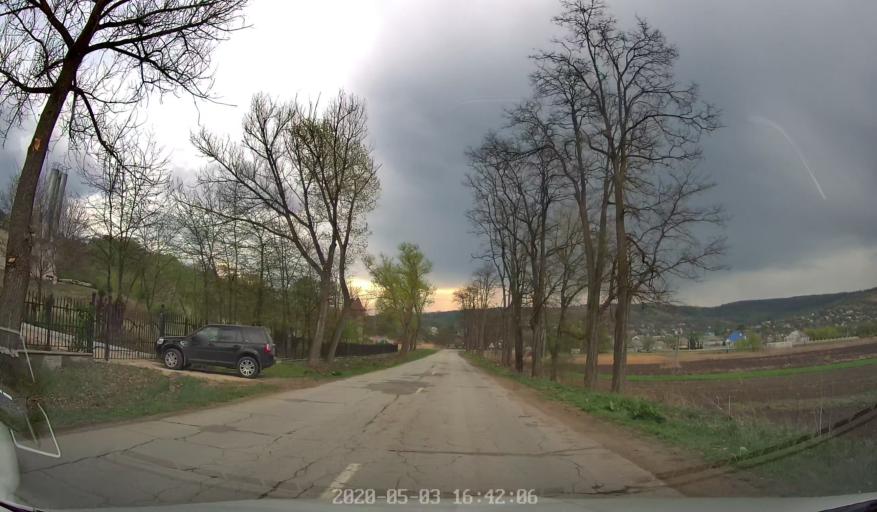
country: MD
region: Stinga Nistrului
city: Bucovat
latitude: 47.1616
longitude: 28.4166
